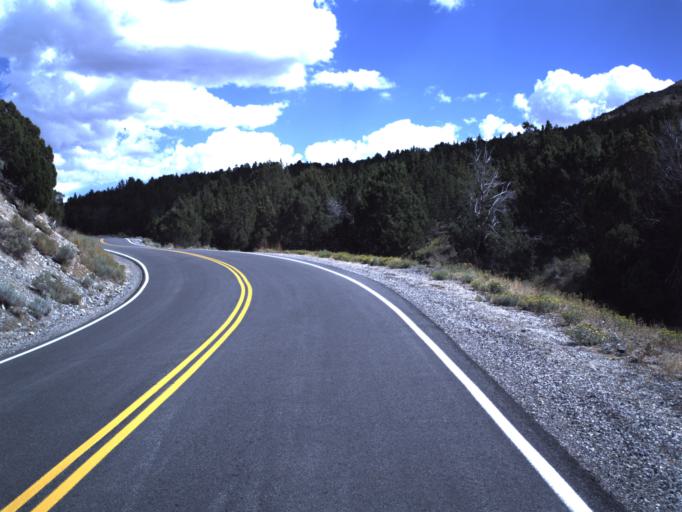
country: US
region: Utah
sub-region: Tooele County
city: Grantsville
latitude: 40.3440
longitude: -112.5830
